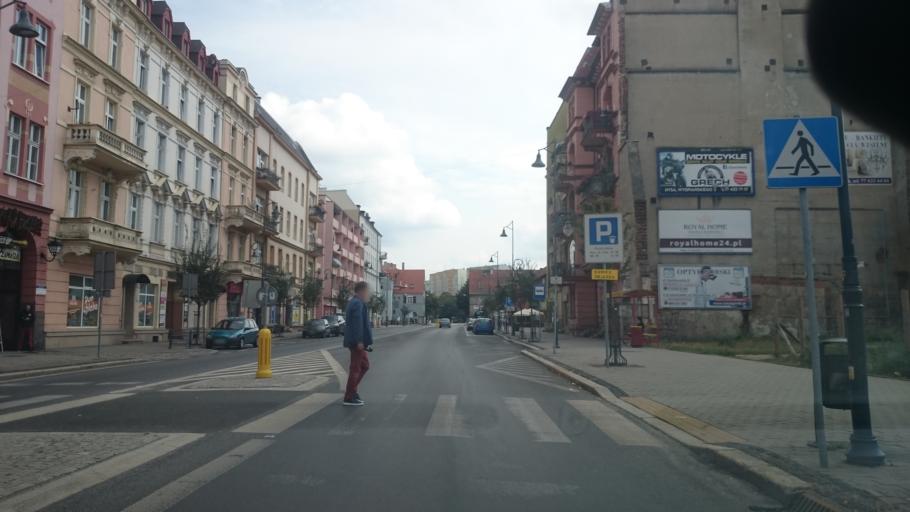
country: PL
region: Opole Voivodeship
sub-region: Powiat nyski
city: Nysa
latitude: 50.4706
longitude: 17.3365
